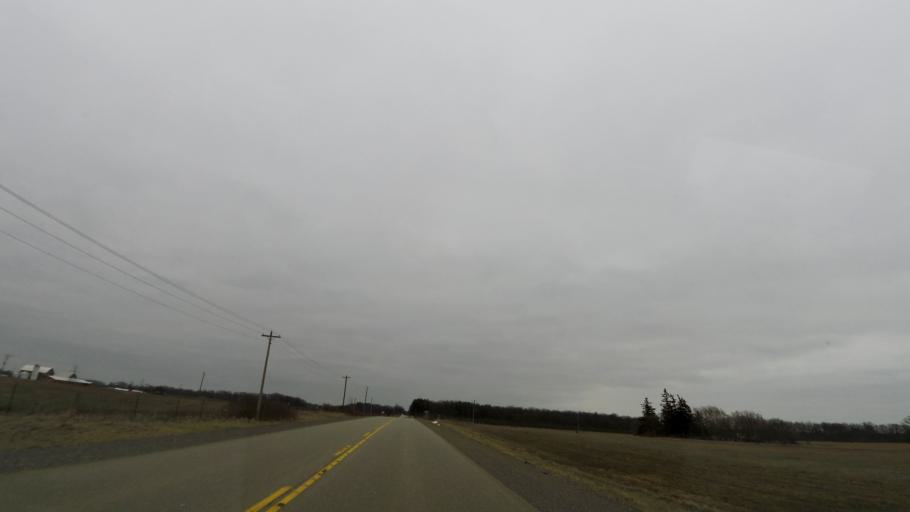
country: CA
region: Ontario
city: Brantford
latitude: 43.1096
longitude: -80.1589
